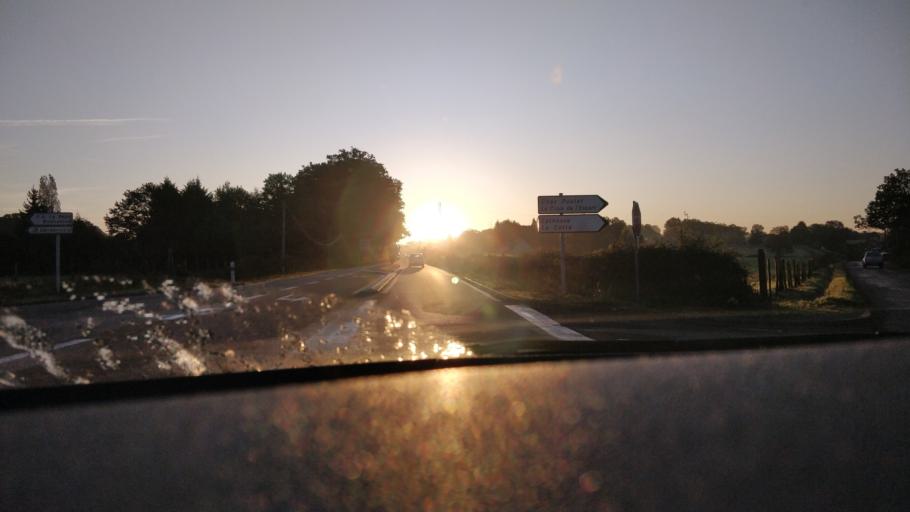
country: FR
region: Limousin
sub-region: Departement de la Haute-Vienne
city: Saint-Just-le-Martel
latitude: 45.8465
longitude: 1.3696
